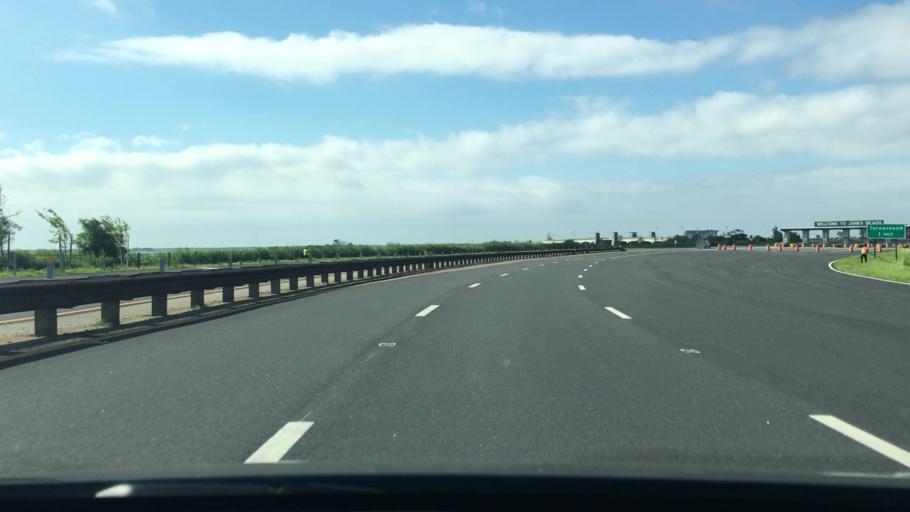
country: US
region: New York
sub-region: Nassau County
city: Seaford
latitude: 40.6216
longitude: -73.5008
